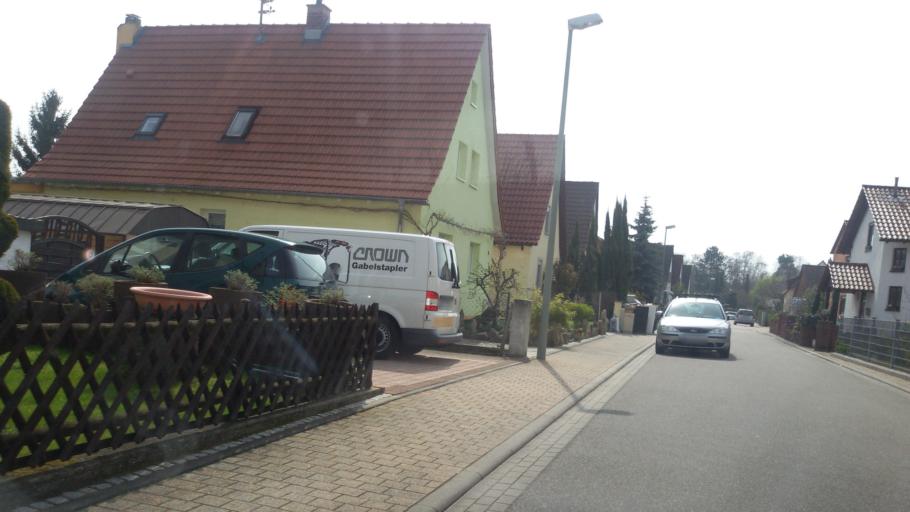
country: DE
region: Rheinland-Pfalz
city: Birkenheide
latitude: 49.4824
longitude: 8.2694
